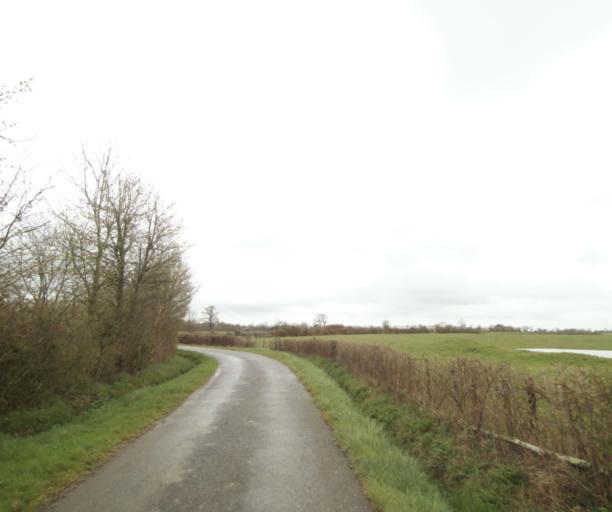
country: FR
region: Pays de la Loire
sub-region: Departement de la Loire-Atlantique
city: Bouvron
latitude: 47.4536
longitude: -1.8877
